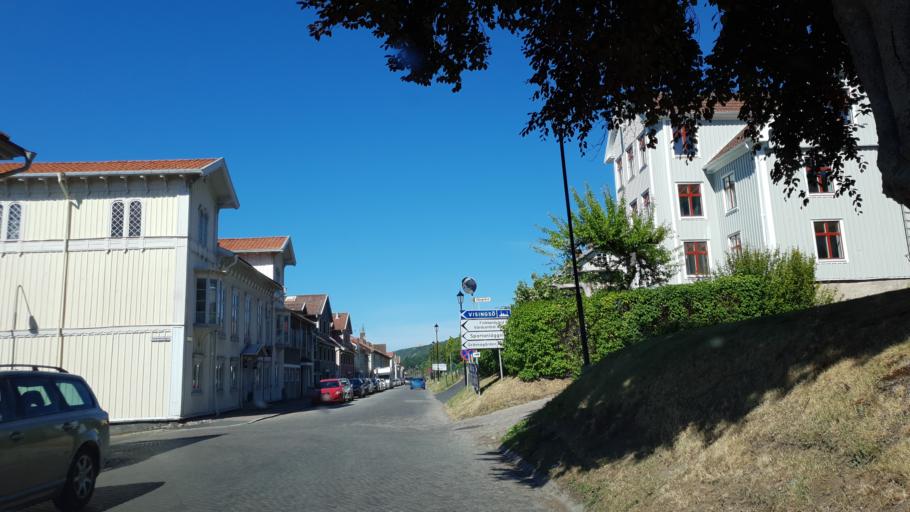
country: SE
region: Joenkoeping
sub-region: Jonkopings Kommun
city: Graenna
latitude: 58.0249
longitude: 14.4700
